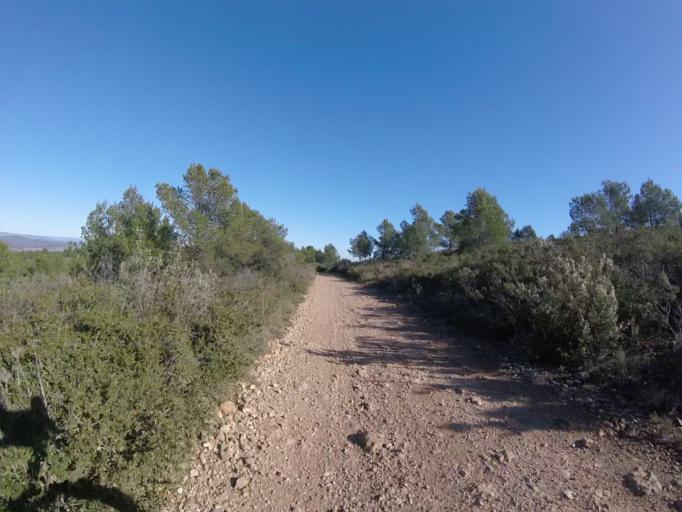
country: ES
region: Valencia
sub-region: Provincia de Castello
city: Orpesa/Oropesa del Mar
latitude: 40.0922
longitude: 0.1050
